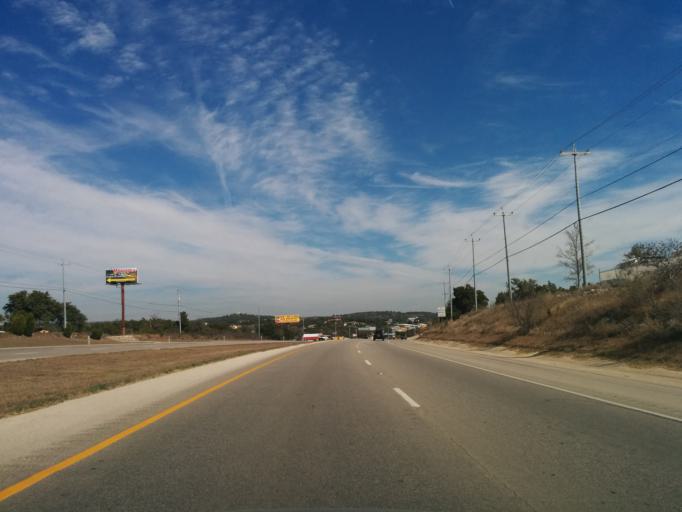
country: US
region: Texas
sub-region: Comal County
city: Bulverde
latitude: 29.7379
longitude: -98.4385
